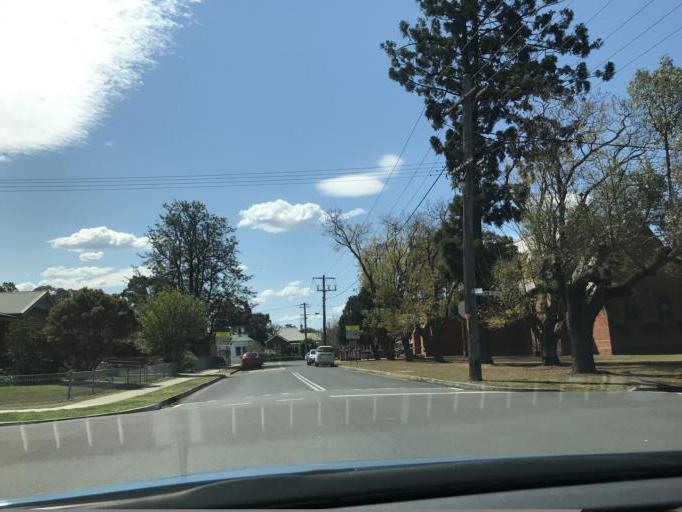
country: AU
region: New South Wales
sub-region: Singleton
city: Singleton
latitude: -32.5648
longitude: 151.1727
